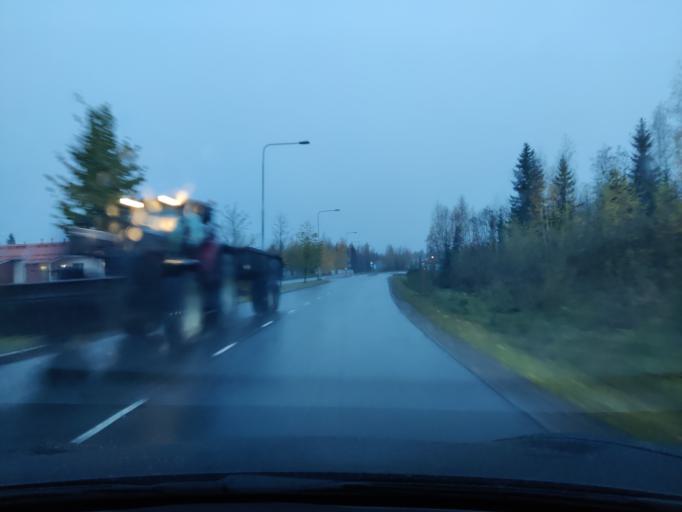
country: FI
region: Northern Savo
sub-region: Kuopio
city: Kuopio
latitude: 62.8268
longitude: 27.6993
